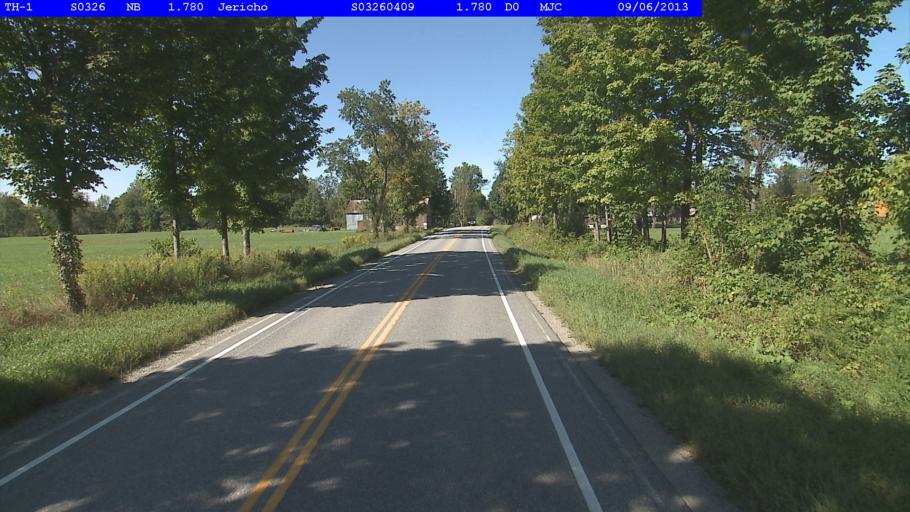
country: US
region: Vermont
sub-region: Chittenden County
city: Jericho
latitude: 44.5022
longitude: -72.9540
